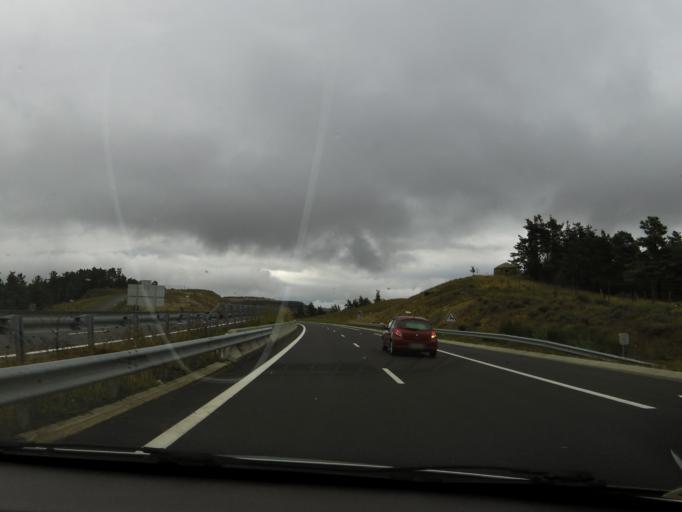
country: FR
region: Languedoc-Roussillon
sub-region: Departement de la Lozere
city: Chirac
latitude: 44.4992
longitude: 3.2531
